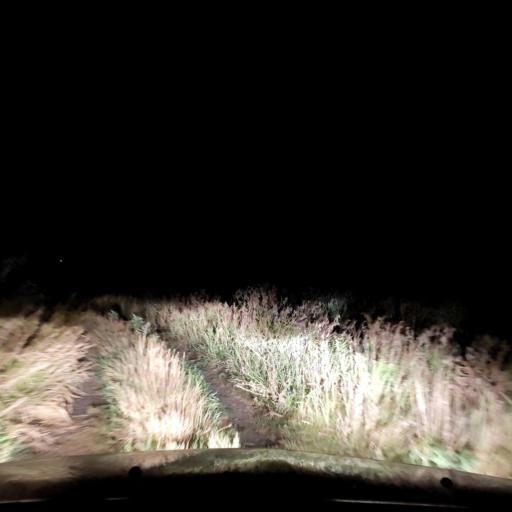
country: RU
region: Voronezj
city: Shilovo
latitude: 51.5934
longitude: 39.0248
